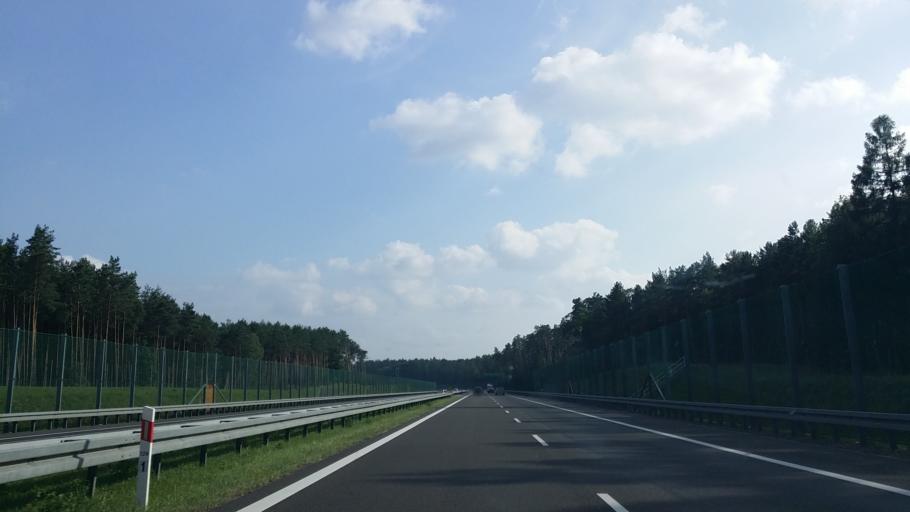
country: PL
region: Lubusz
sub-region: Powiat miedzyrzecki
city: Miedzyrzecz
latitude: 52.4953
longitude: 15.5524
